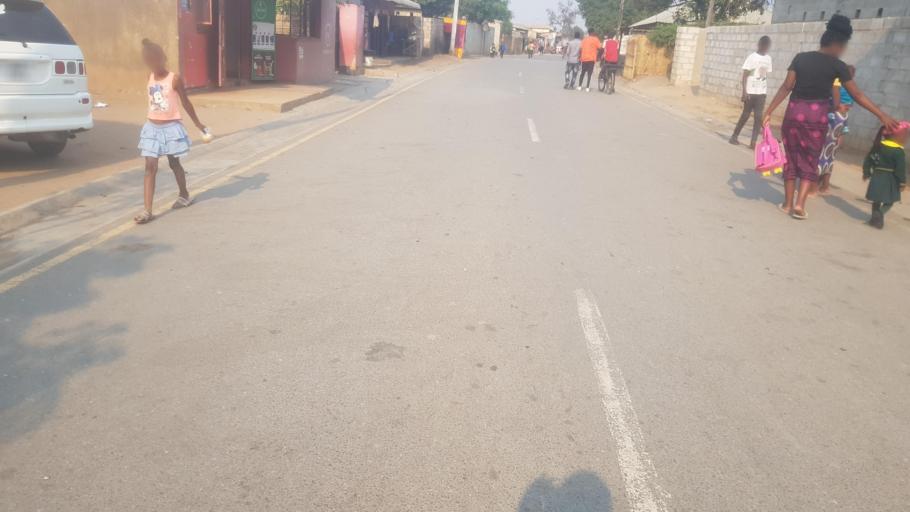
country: ZM
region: Lusaka
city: Lusaka
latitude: -15.4409
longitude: 28.3807
